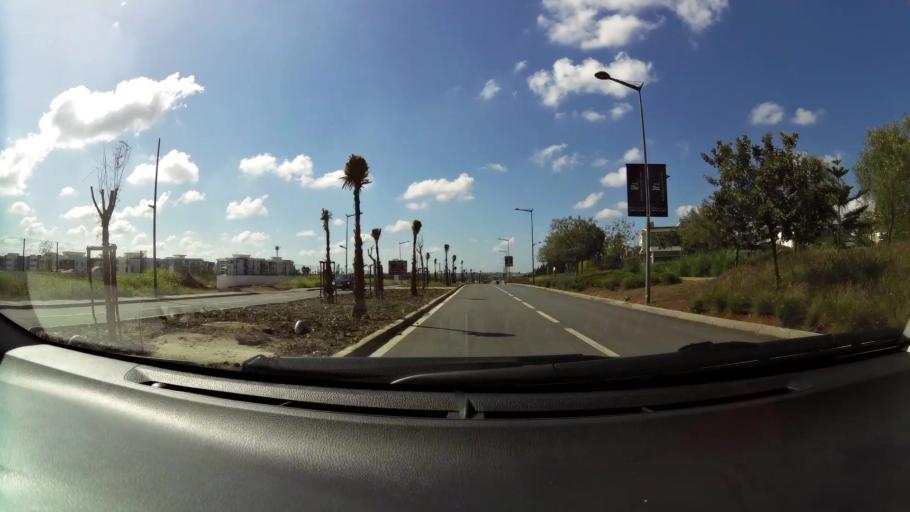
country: MA
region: Grand Casablanca
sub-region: Nouaceur
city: Bouskoura
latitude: 33.4751
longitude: -7.6016
